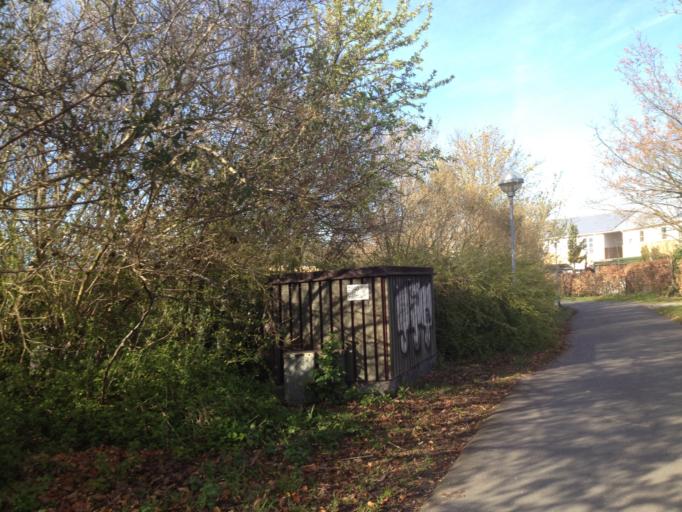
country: DK
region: Capital Region
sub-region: Ballerup Kommune
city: Ballerup
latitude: 55.7472
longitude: 12.3780
